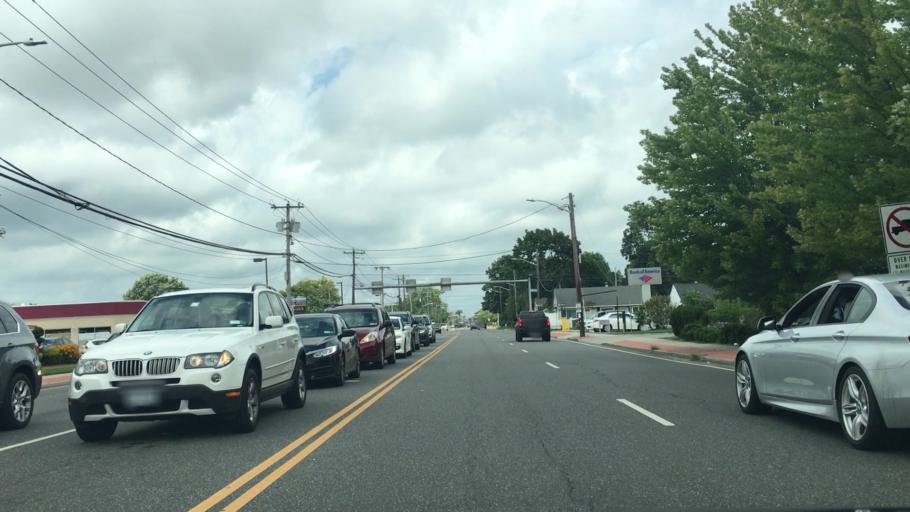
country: US
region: New York
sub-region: Nassau County
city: Hicksville
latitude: 40.7700
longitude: -73.5012
